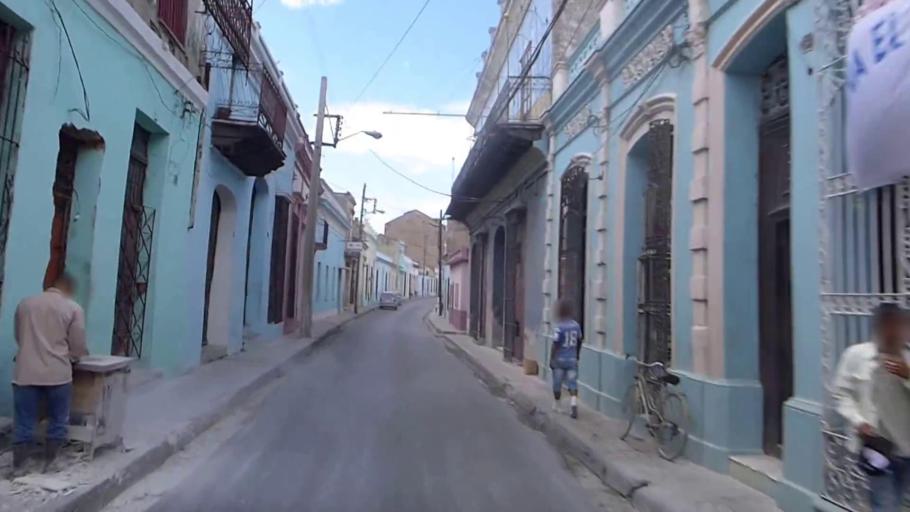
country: CU
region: Camaguey
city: Camaguey
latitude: 21.3844
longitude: -77.9194
